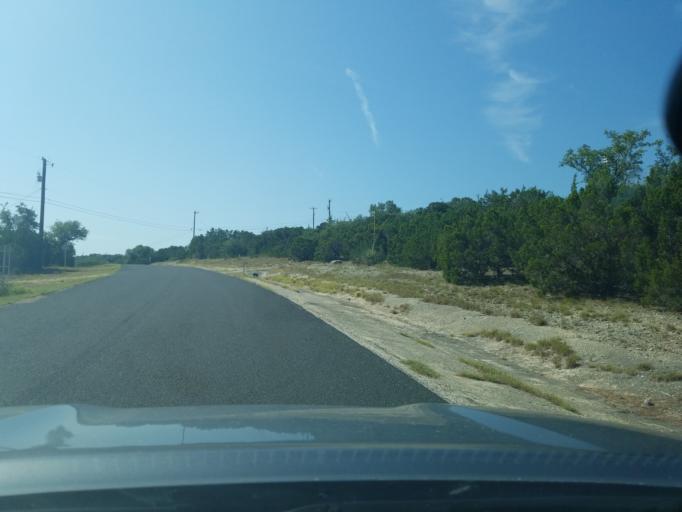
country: US
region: Texas
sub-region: Bexar County
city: Timberwood Park
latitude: 29.6775
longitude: -98.5122
